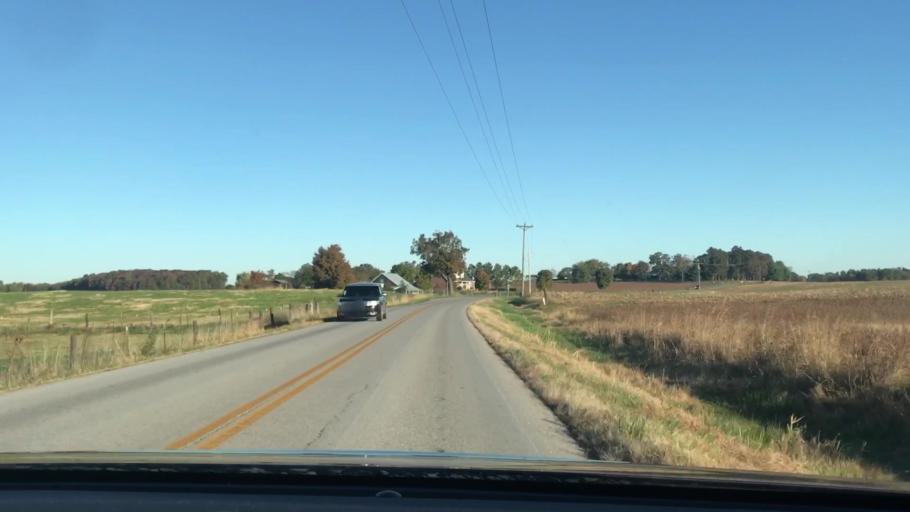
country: US
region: Kentucky
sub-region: Logan County
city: Auburn
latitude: 36.8105
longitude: -86.6380
